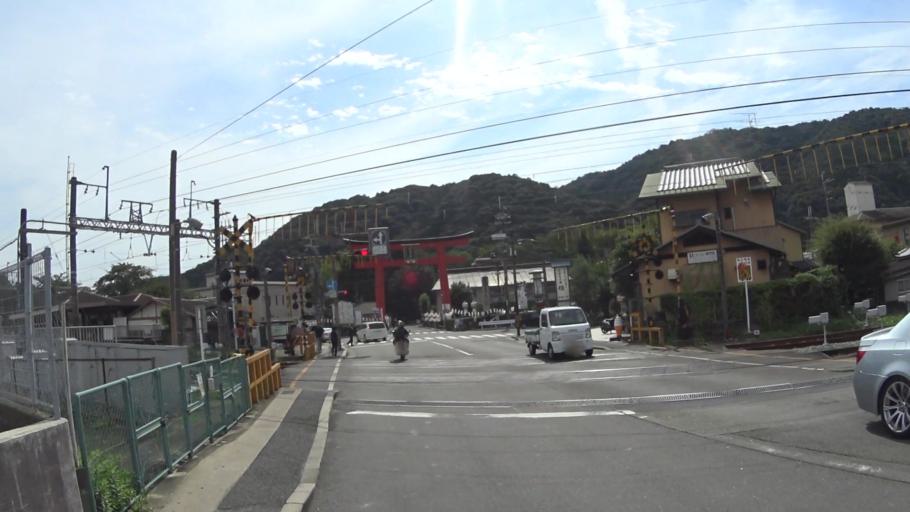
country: JP
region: Kyoto
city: Muko
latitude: 35.0010
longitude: 135.6882
